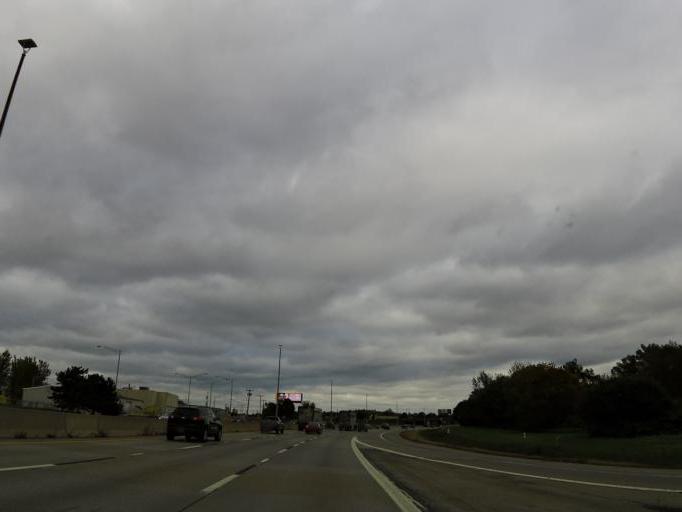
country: US
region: New York
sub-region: Erie County
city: Sloan
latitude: 42.8746
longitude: -78.8127
